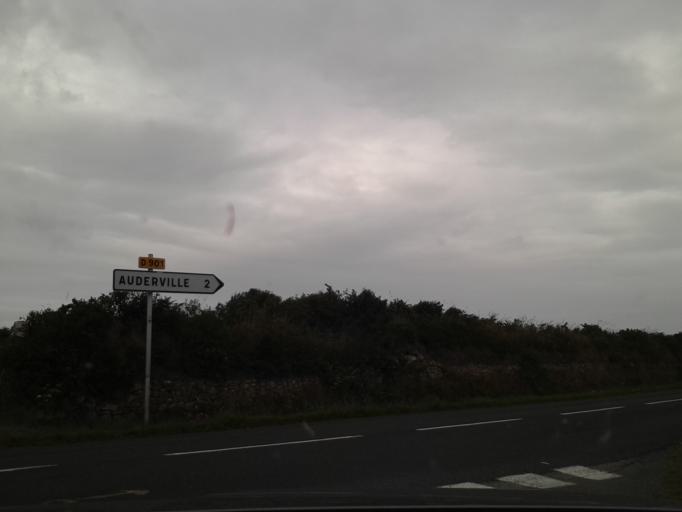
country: FR
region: Lower Normandy
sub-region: Departement de la Manche
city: Beaumont-Hague
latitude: 49.6961
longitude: -1.9211
